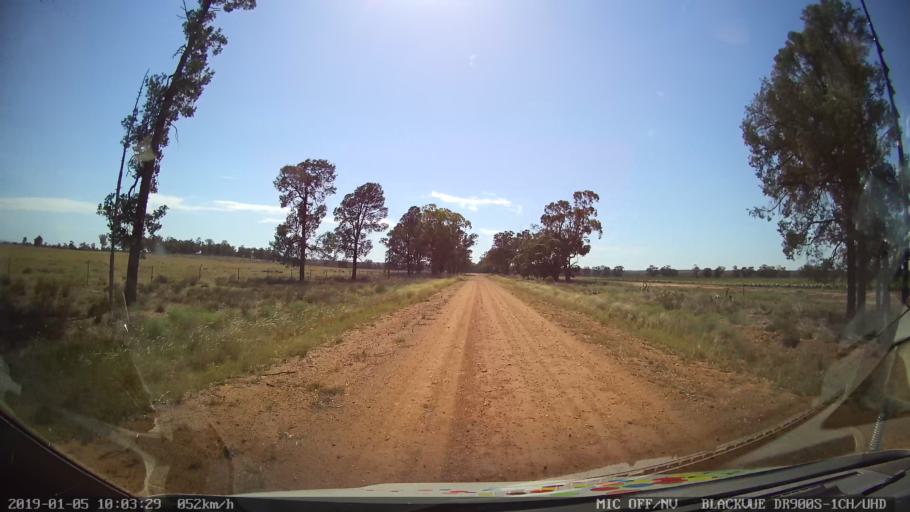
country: AU
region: New South Wales
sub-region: Gilgandra
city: Gilgandra
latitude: -31.6719
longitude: 148.8525
